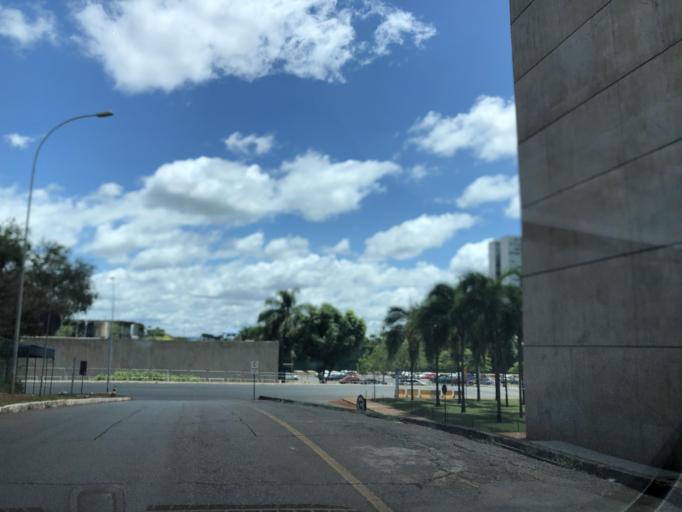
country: BR
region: Federal District
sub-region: Brasilia
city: Brasilia
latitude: -15.8024
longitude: -47.8665
